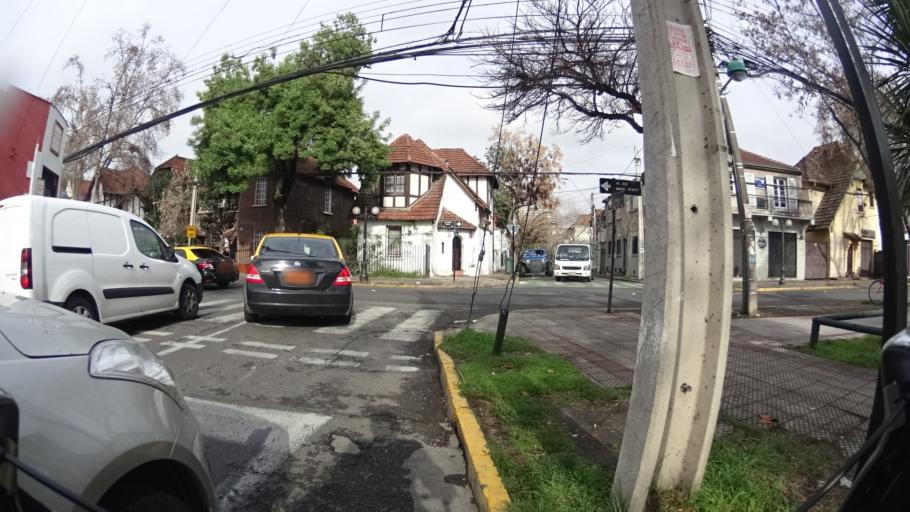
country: CL
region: Santiago Metropolitan
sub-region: Provincia de Santiago
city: Santiago
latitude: -33.4342
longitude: -70.6230
